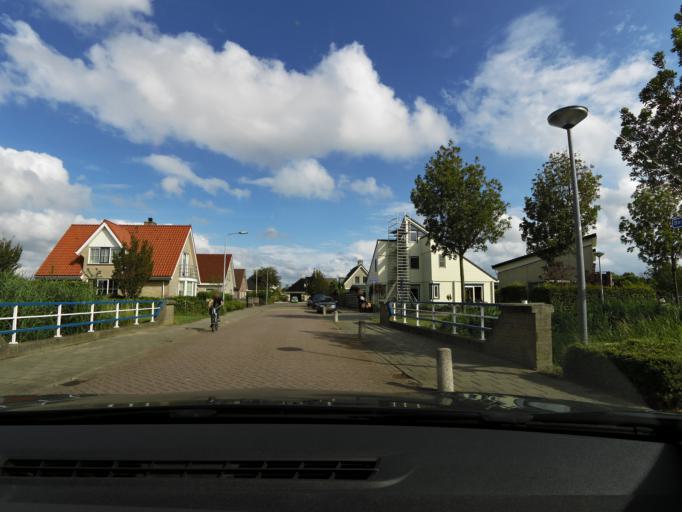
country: NL
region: South Holland
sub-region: Gemeente Goeree-Overflakkee
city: Goedereede
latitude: 51.8206
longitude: 3.9860
